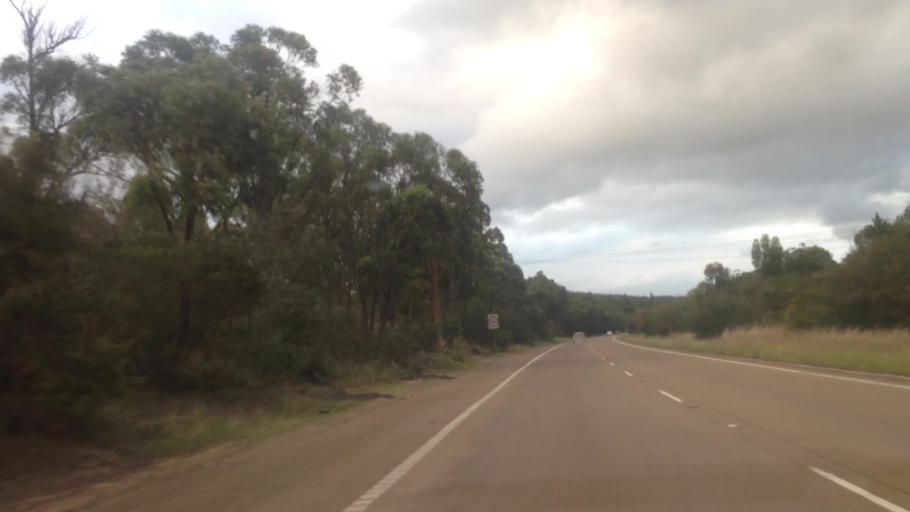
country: AU
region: New South Wales
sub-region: Wyong Shire
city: Charmhaven
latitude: -33.1754
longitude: 151.4666
